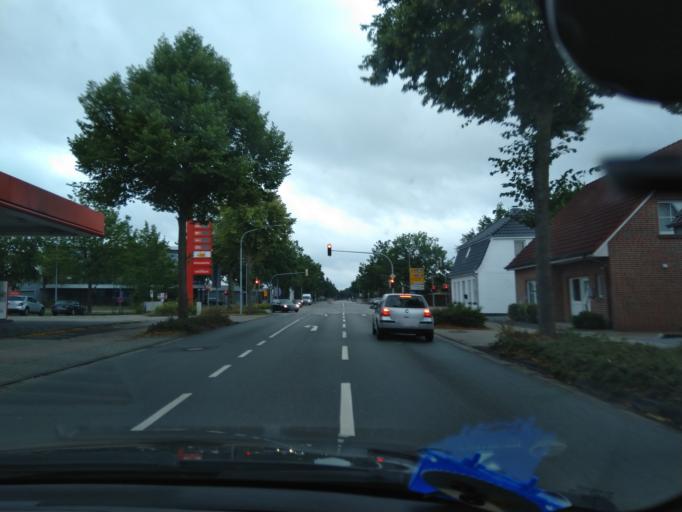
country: DE
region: Lower Saxony
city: Nordhorn
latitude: 52.4198
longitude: 7.0832
